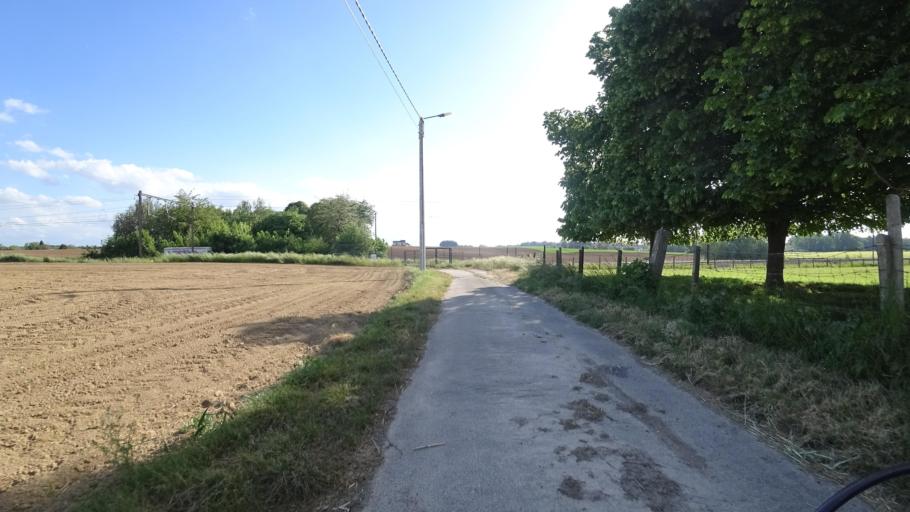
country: BE
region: Wallonia
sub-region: Province de Namur
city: Gembloux
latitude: 50.5385
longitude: 4.7423
